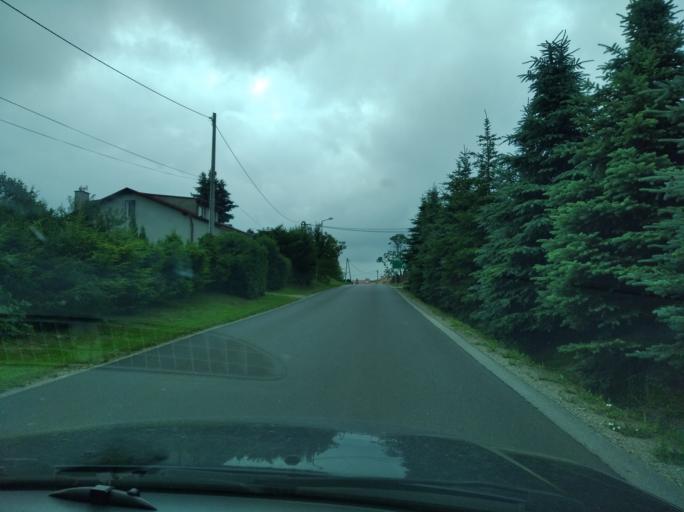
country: PL
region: Subcarpathian Voivodeship
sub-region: Powiat jaroslawski
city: Pawlosiow
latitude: 50.0163
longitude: 22.6424
